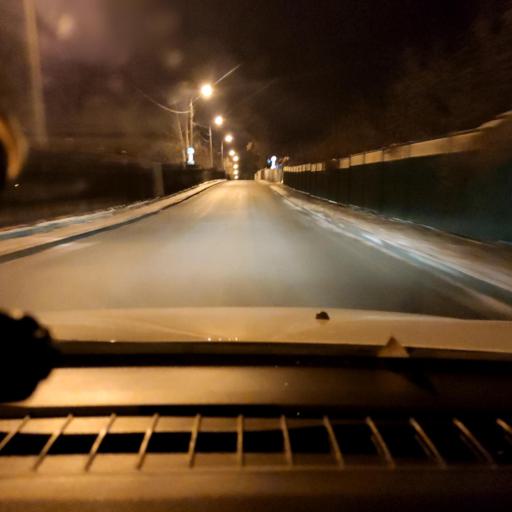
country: RU
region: Samara
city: Samara
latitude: 53.2287
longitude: 50.1734
